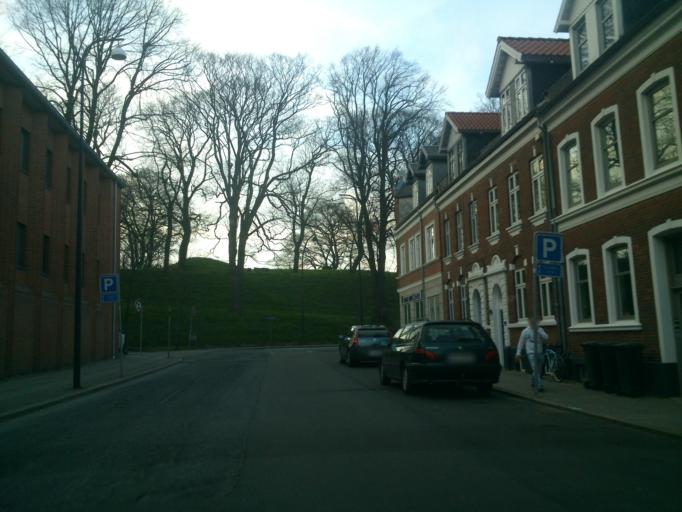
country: DK
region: South Denmark
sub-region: Fredericia Kommune
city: Fredericia
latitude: 55.5691
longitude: 9.7592
